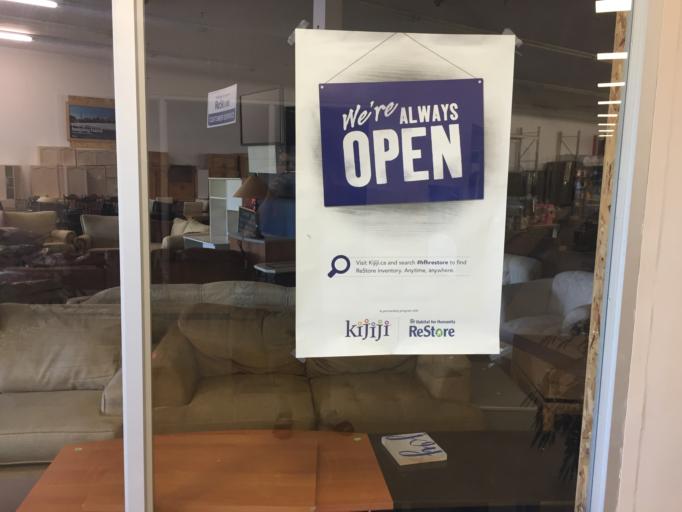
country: CA
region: Ontario
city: Oshawa
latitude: 43.8939
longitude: -78.8679
